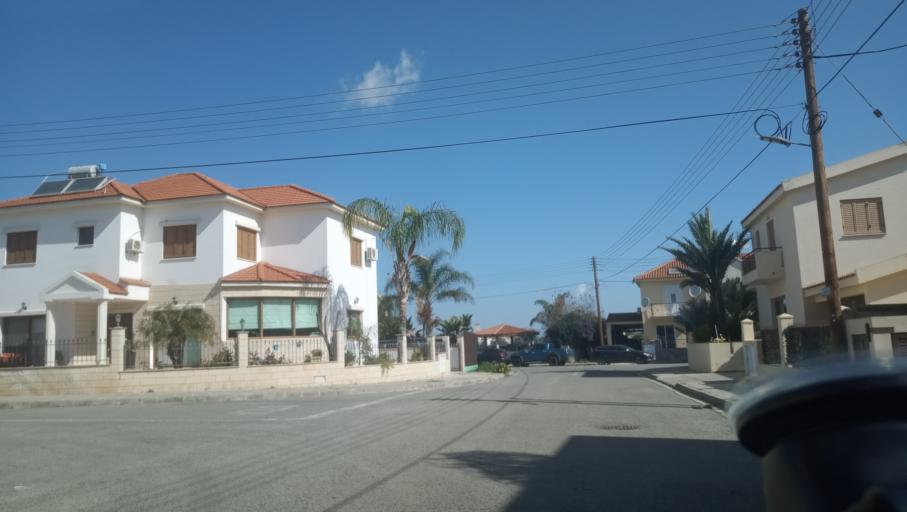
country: CY
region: Lefkosia
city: Tseri
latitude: 35.0907
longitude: 33.3085
